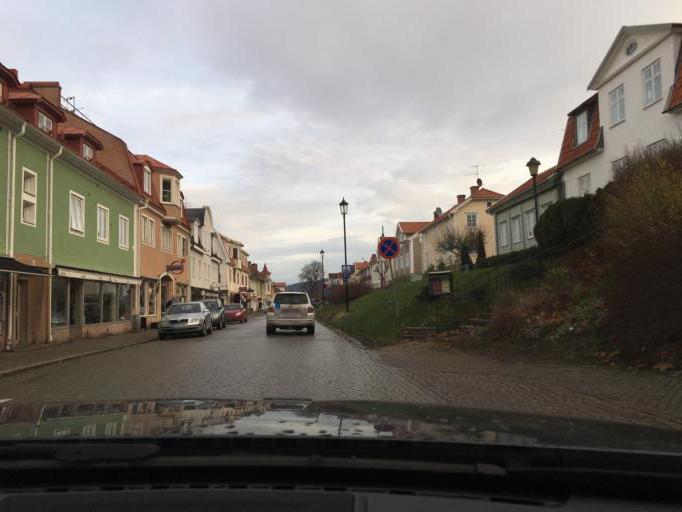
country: SE
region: Joenkoeping
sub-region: Jonkopings Kommun
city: Graenna
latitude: 58.0233
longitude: 14.4680
